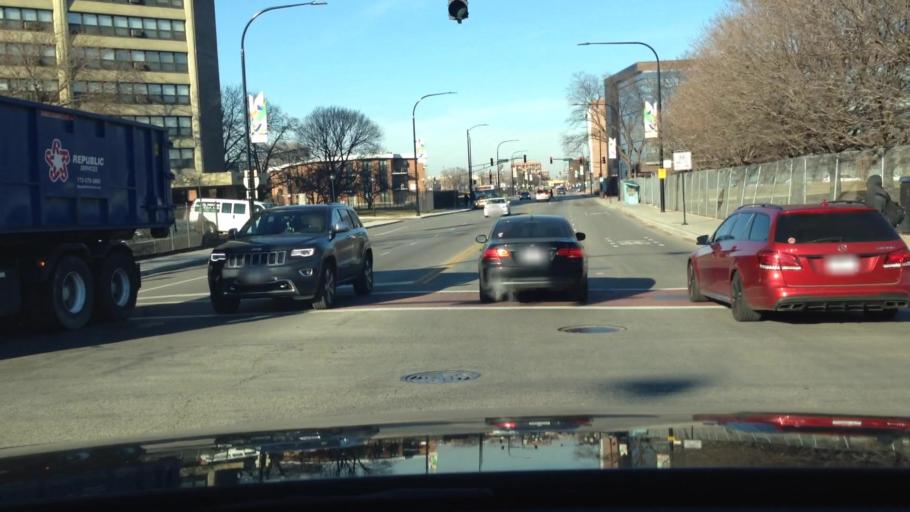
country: US
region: Illinois
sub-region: Cook County
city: Chicago
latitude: 41.8761
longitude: -87.6765
